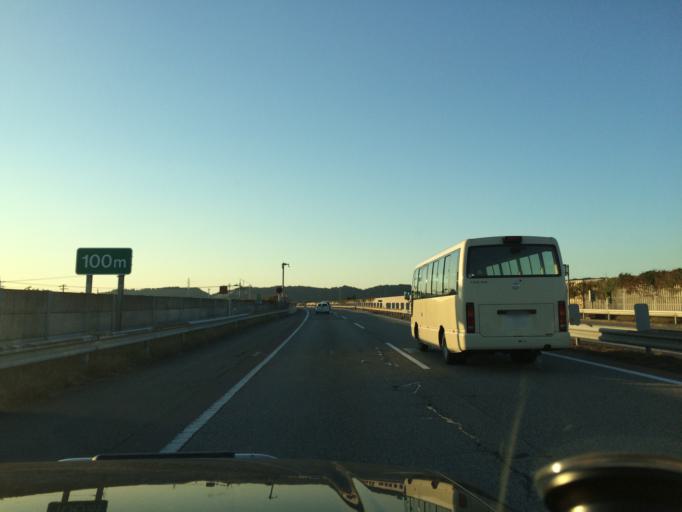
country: JP
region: Toyama
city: Toyama-shi
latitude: 36.6706
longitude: 137.1785
